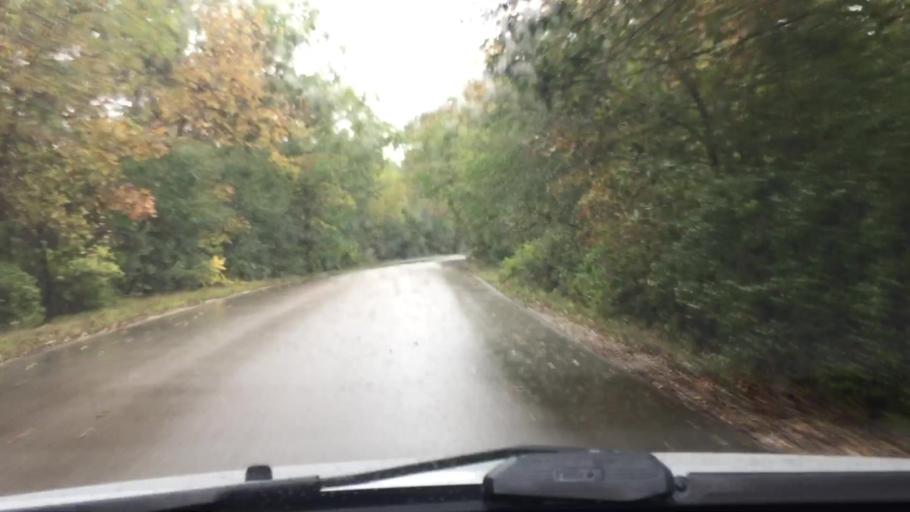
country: US
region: Wisconsin
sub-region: Waukesha County
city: North Prairie
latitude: 42.9307
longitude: -88.4537
